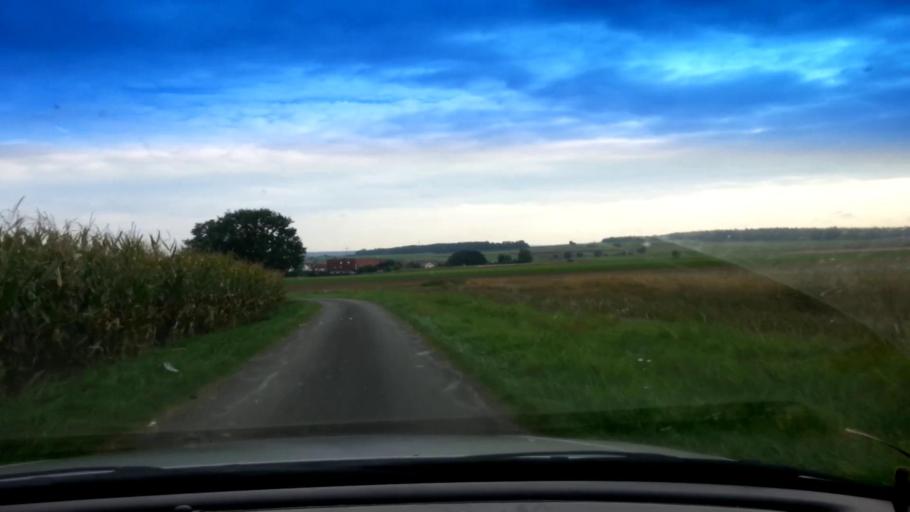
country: DE
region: Bavaria
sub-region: Upper Franconia
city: Memmelsdorf
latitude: 49.9652
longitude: 10.9528
